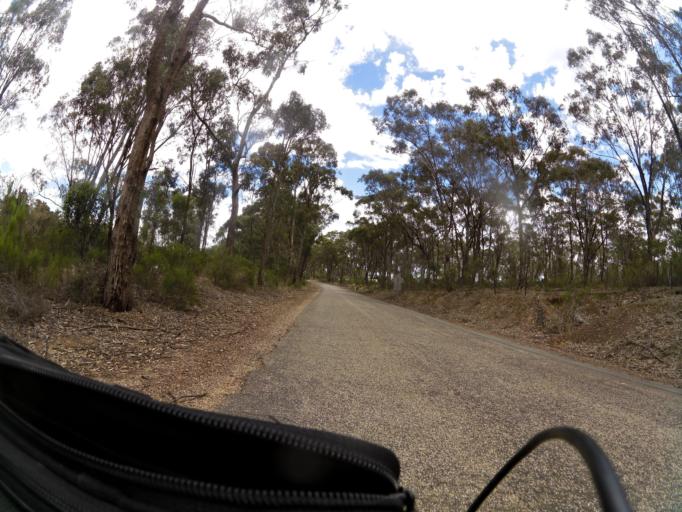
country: AU
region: Victoria
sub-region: Greater Shepparton
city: Shepparton
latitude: -36.6915
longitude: 145.1761
